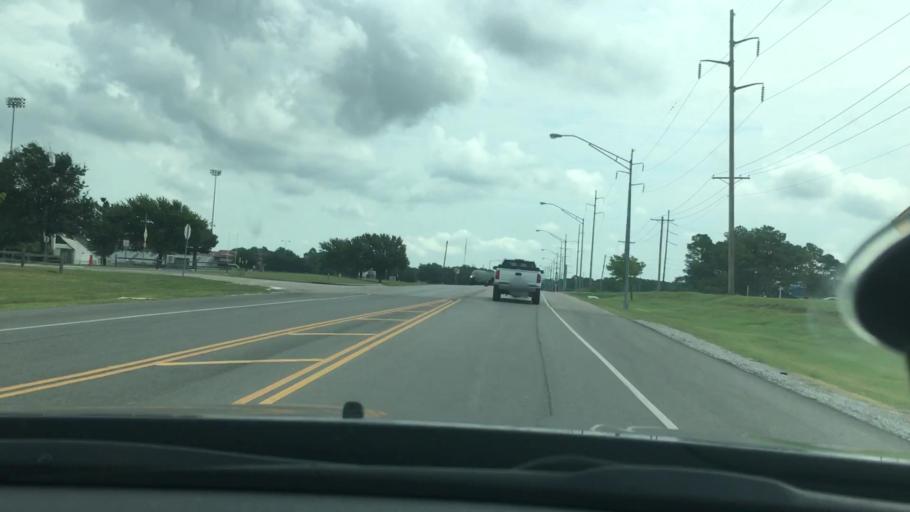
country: US
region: Oklahoma
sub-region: Carter County
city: Ardmore
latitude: 34.2029
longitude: -97.1393
